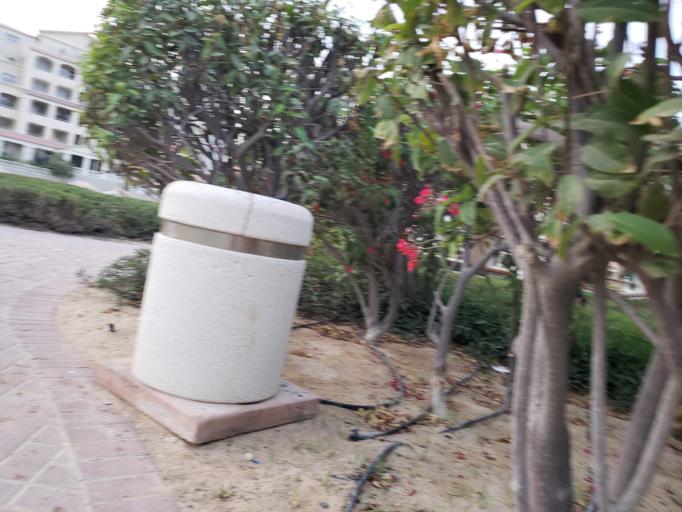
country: AE
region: Dubai
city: Dubai
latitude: 25.0415
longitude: 55.2324
